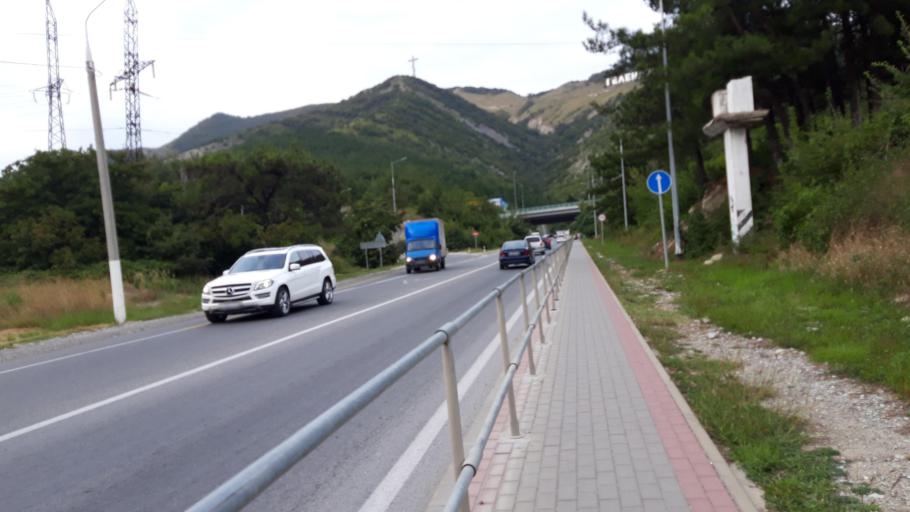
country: RU
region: Krasnodarskiy
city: Gelendzhik
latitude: 44.5741
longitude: 38.0913
